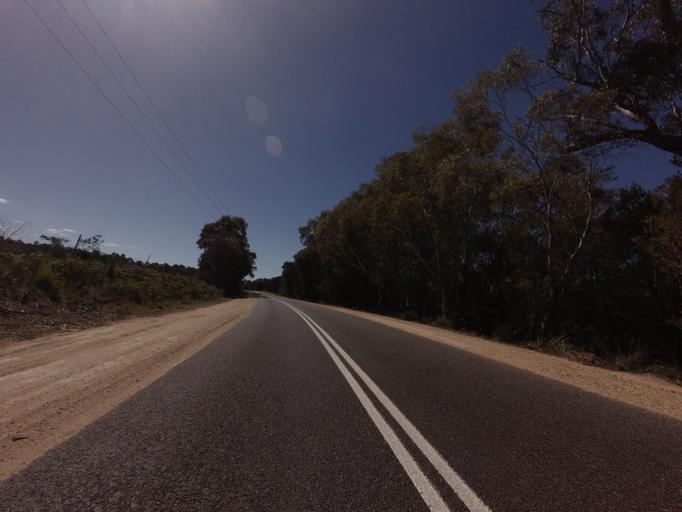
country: AU
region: Tasmania
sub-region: Break O'Day
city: St Helens
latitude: -41.8322
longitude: 148.2576
